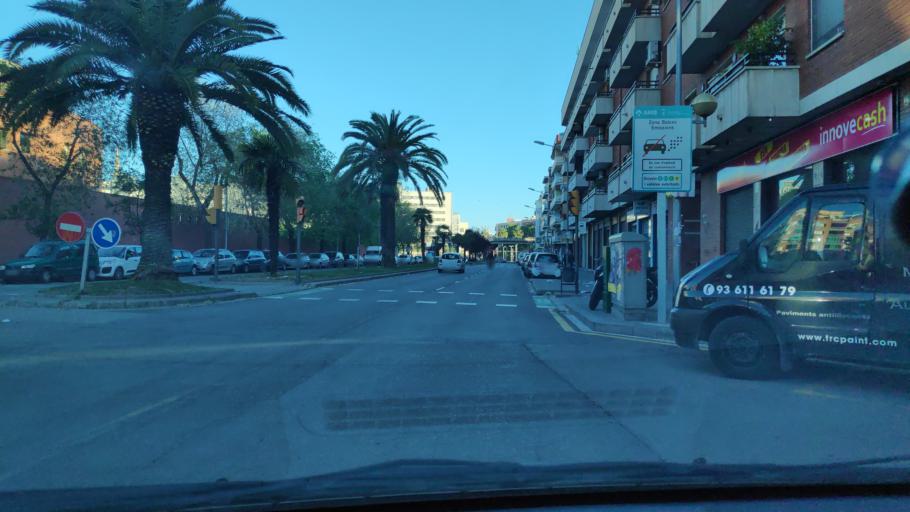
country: ES
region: Catalonia
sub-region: Provincia de Barcelona
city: Sant Adria de Besos
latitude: 41.4313
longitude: 2.2202
